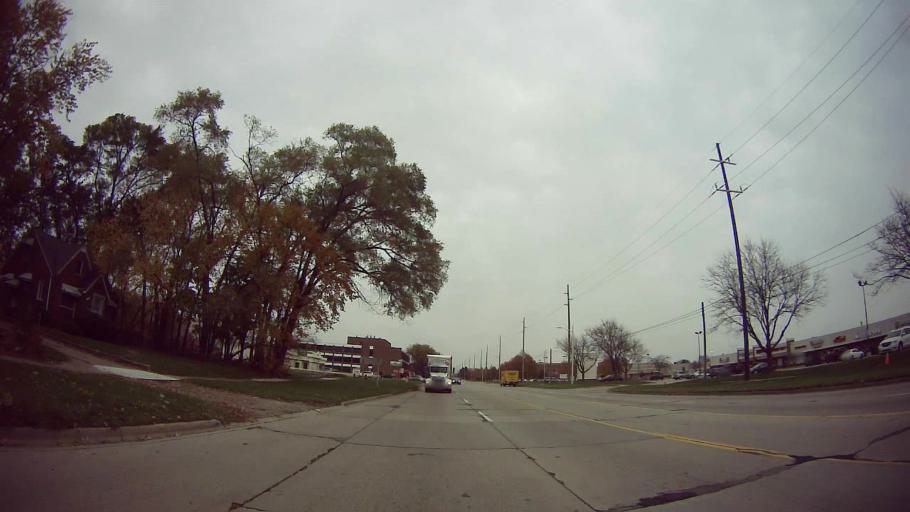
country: US
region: Michigan
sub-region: Oakland County
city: Madison Heights
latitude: 42.4916
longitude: -83.0852
